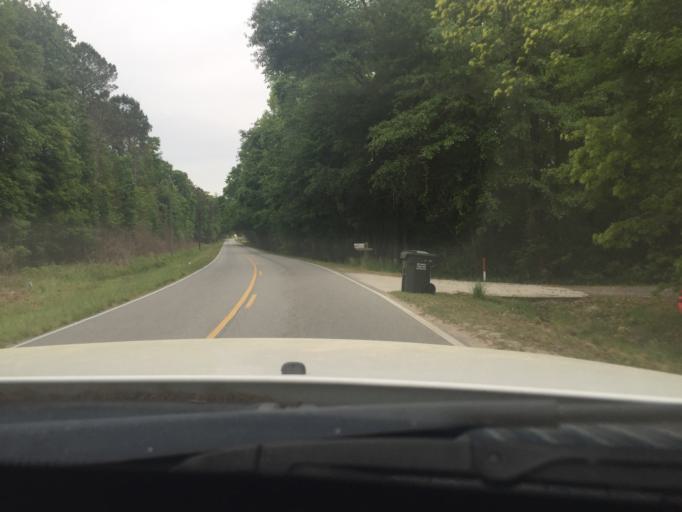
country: US
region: Georgia
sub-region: Chatham County
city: Georgetown
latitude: 31.9785
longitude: -81.2500
